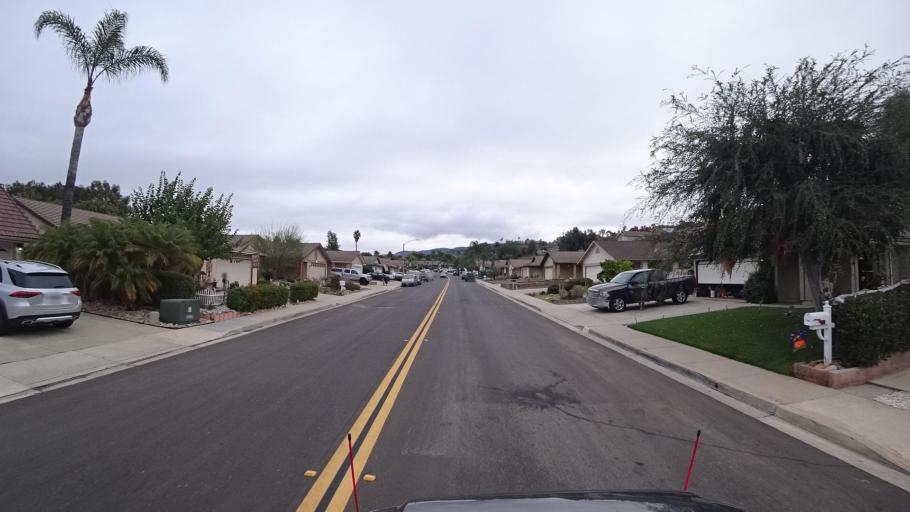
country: US
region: California
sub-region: San Diego County
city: Rancho San Diego
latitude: 32.7559
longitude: -116.9175
